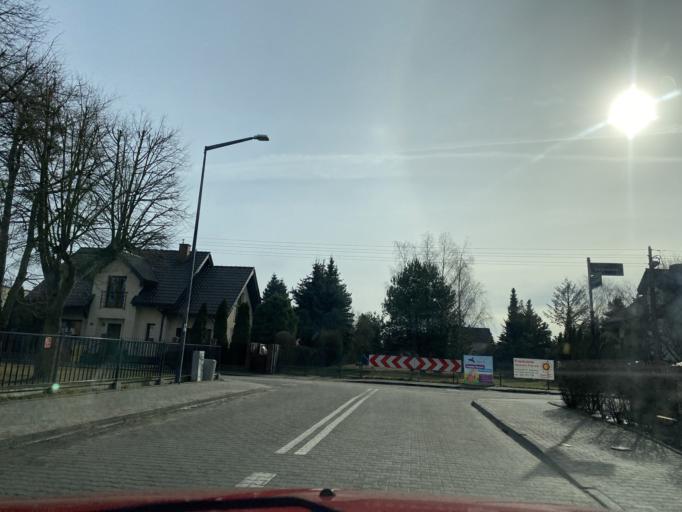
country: PL
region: Greater Poland Voivodeship
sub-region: Powiat poznanski
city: Baranowo
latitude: 52.4365
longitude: 16.8211
